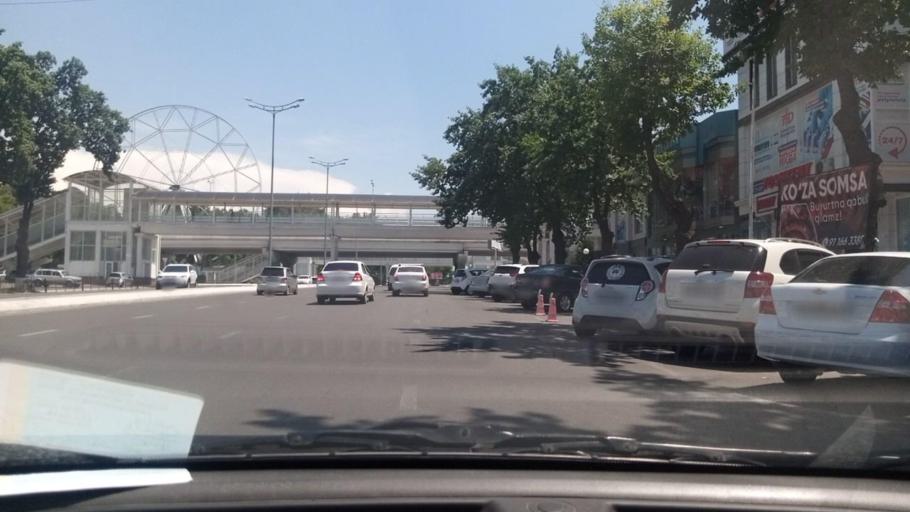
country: UZ
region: Toshkent Shahri
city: Tashkent
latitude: 41.2829
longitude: 69.2111
